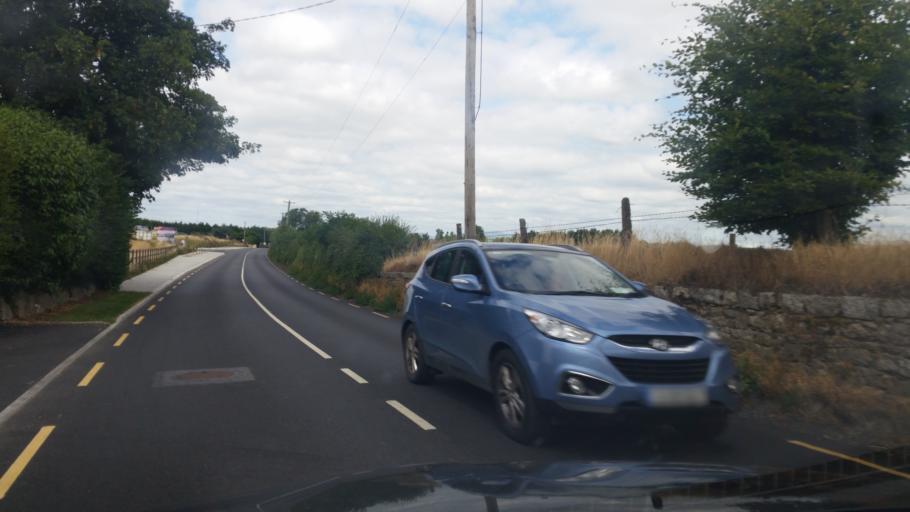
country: IE
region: Leinster
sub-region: County Carlow
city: Tullow
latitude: 52.7925
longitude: -6.7508
